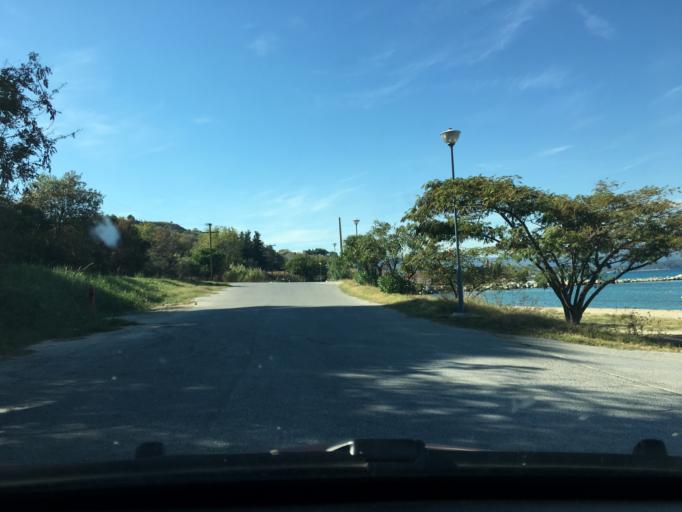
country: GR
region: Central Macedonia
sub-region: Nomos Chalkidikis
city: Ierissos
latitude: 40.3935
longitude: 23.8923
